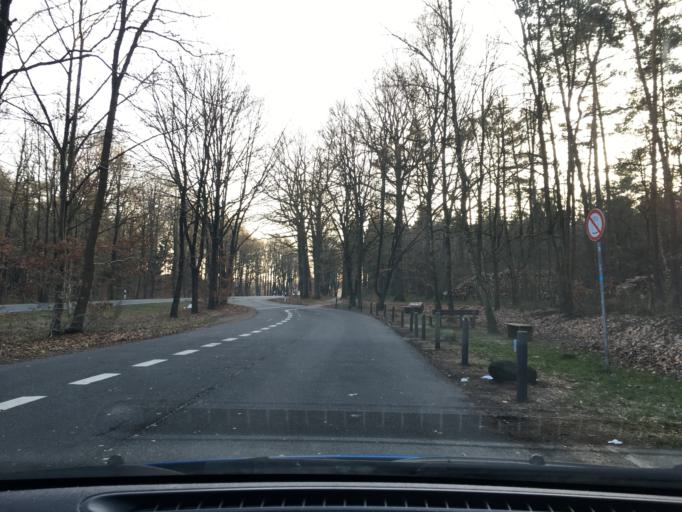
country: DE
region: Lower Saxony
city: Suderburg
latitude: 52.8385
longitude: 10.4872
